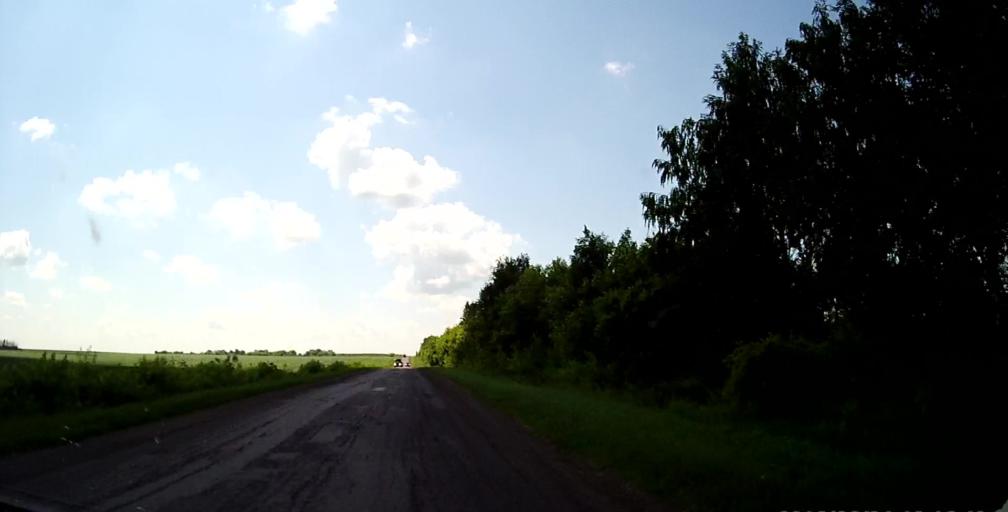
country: RU
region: Lipetsk
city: Chaplygin
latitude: 53.2823
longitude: 39.9611
